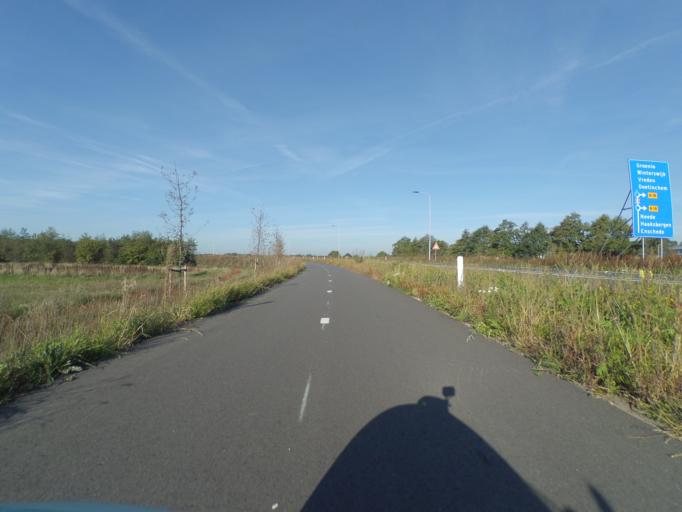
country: NL
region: Gelderland
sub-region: Berkelland
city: Eibergen
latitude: 52.0871
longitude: 6.6371
